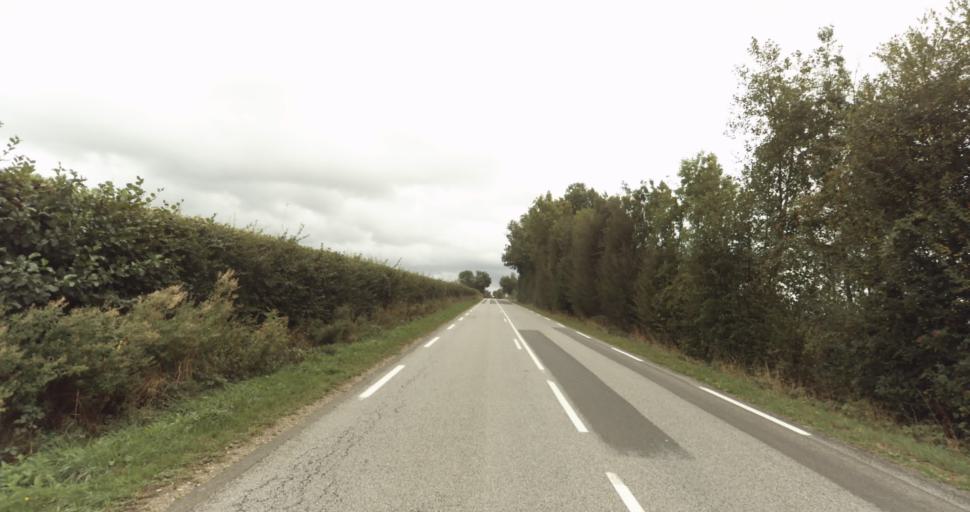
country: FR
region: Lower Normandy
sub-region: Departement de l'Orne
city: Sainte-Gauburge-Sainte-Colombe
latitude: 48.7071
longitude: 0.4362
